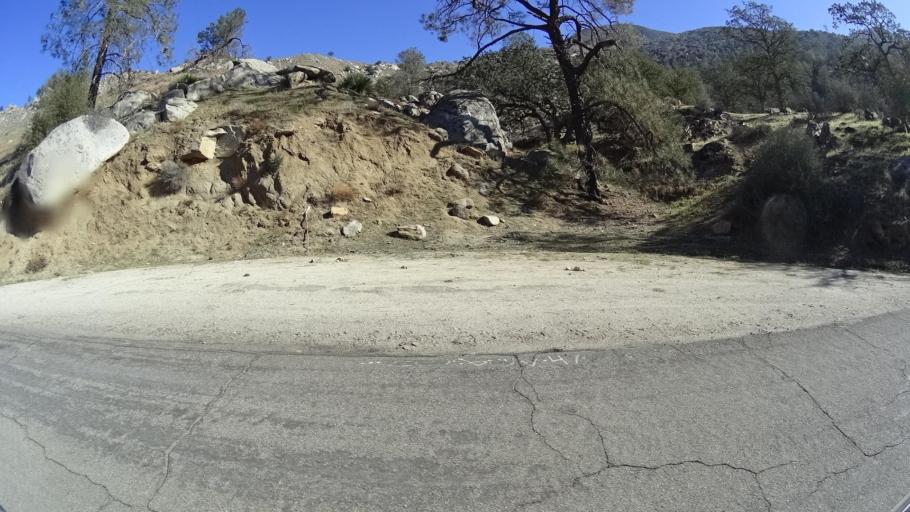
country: US
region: California
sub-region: Kern County
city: Bodfish
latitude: 35.5555
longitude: -118.5800
